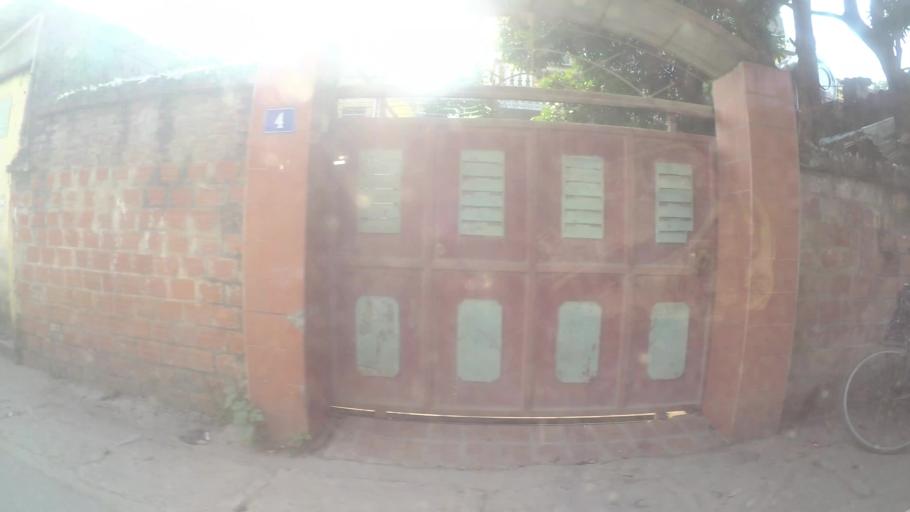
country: VN
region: Ha Noi
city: Ha Dong
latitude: 20.9952
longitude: 105.7558
